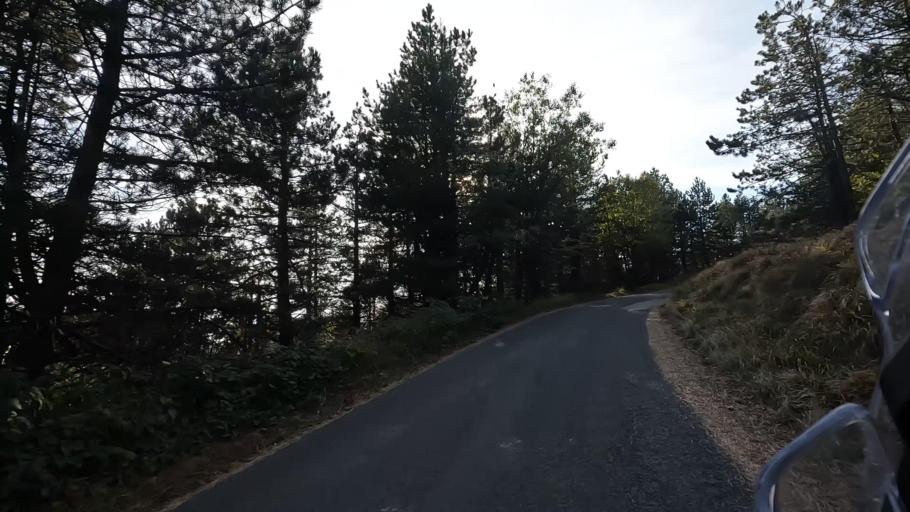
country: IT
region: Liguria
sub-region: Provincia di Genova
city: Sciarborasca
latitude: 44.4301
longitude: 8.5776
